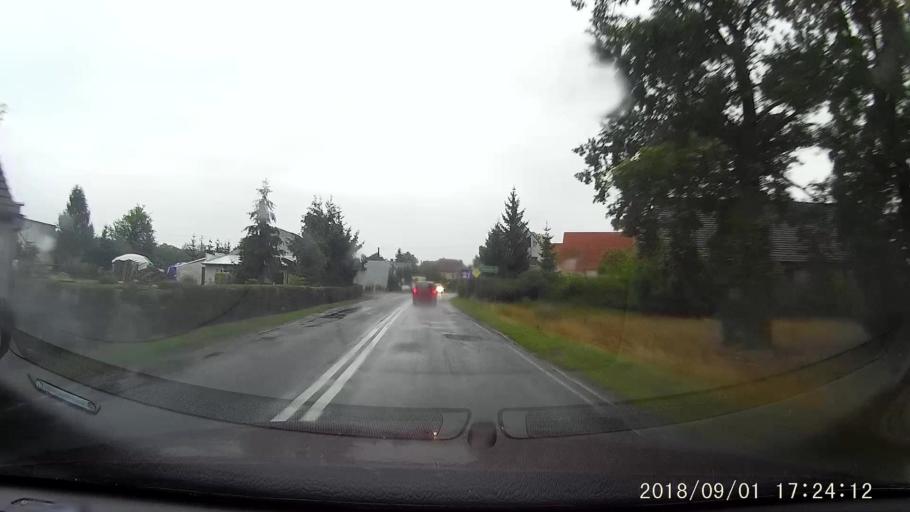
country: PL
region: Lubusz
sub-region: Powiat zaganski
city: Zagan
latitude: 51.6945
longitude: 15.3004
